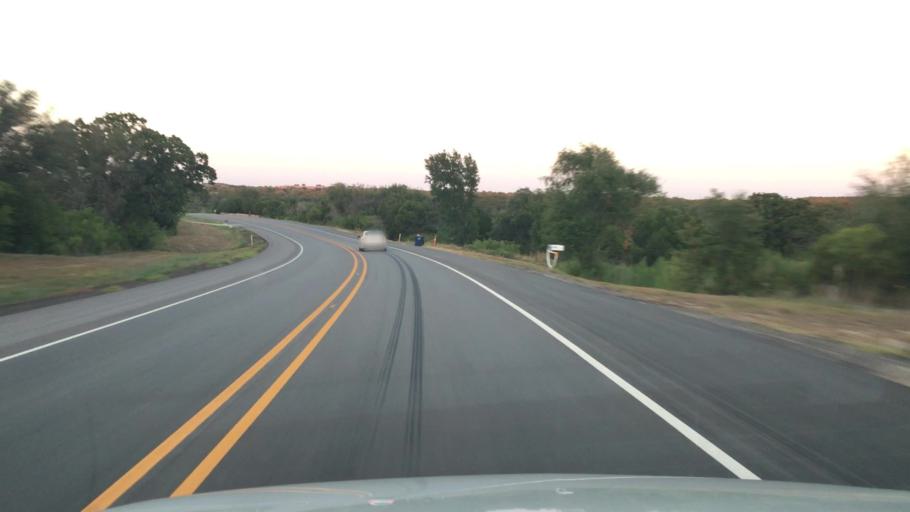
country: US
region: Texas
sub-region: Somervell County
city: Glen Rose
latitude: 32.1909
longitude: -97.8274
